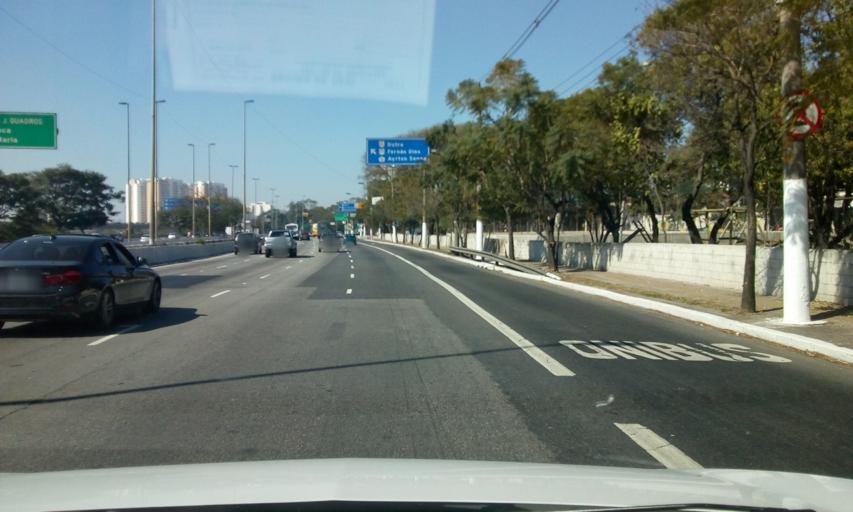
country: BR
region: Sao Paulo
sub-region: Sao Paulo
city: Sao Paulo
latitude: -23.5216
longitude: -46.6152
